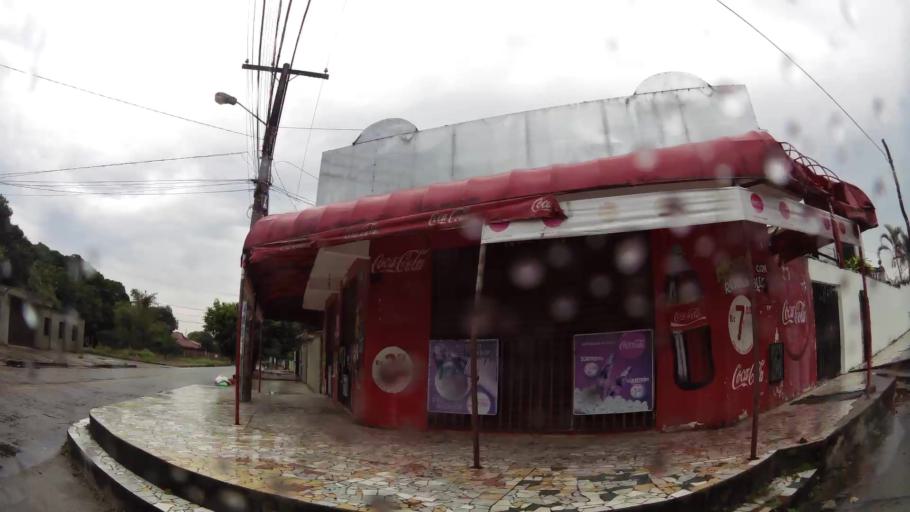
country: BO
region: Santa Cruz
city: Santa Cruz de la Sierra
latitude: -17.7976
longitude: -63.1572
